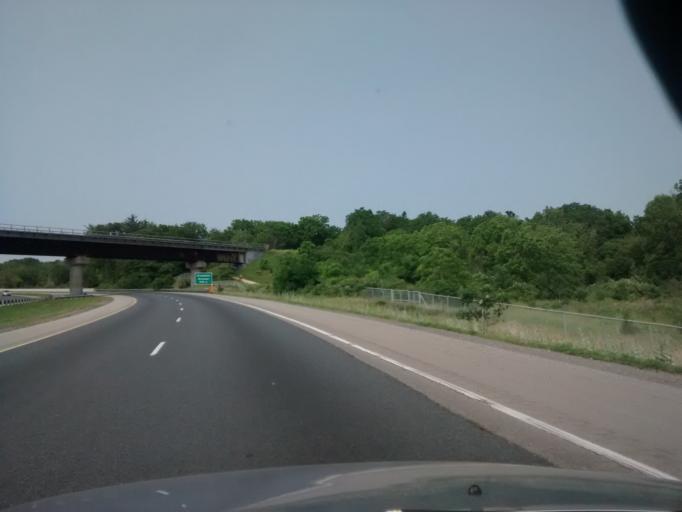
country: CA
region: Ontario
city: Hamilton
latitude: 43.2251
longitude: -79.7939
